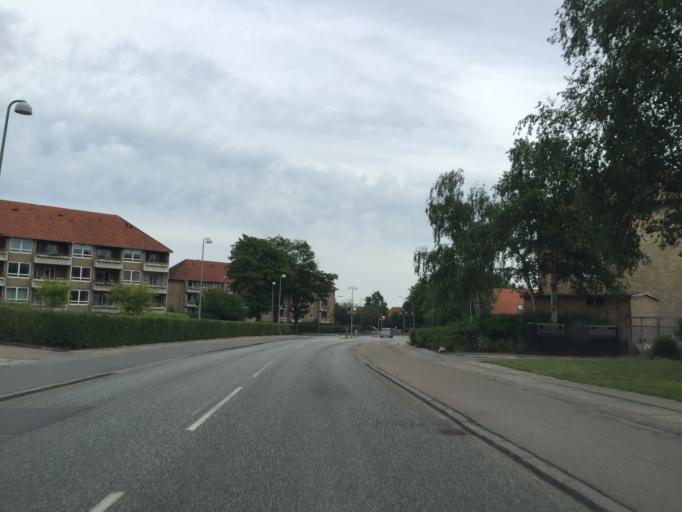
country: DK
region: Capital Region
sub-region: Lyngby-Tarbaek Kommune
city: Kongens Lyngby
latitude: 55.7757
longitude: 12.5134
